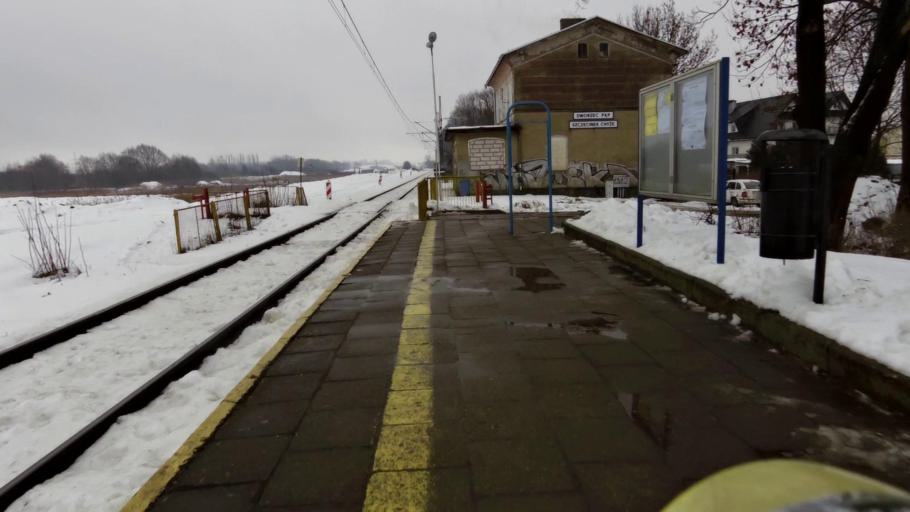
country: PL
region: West Pomeranian Voivodeship
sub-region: Powiat szczecinecki
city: Szczecinek
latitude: 53.7181
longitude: 16.6974
